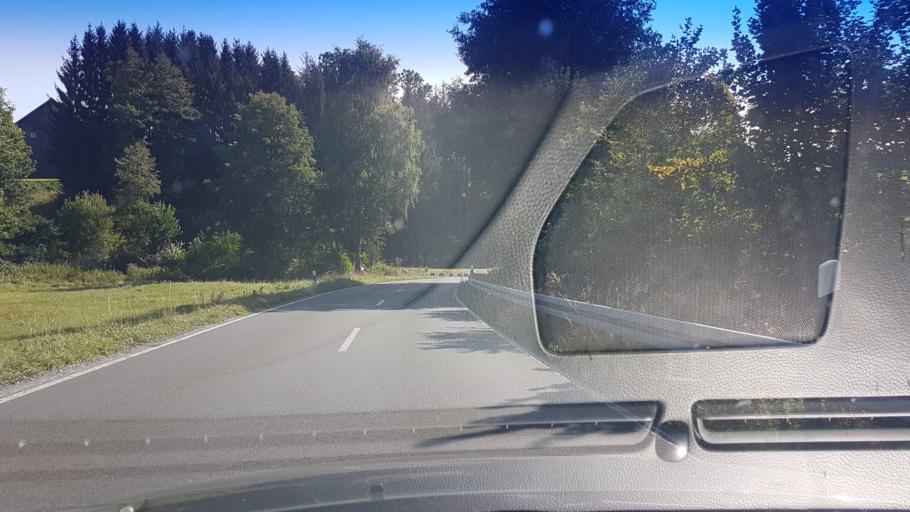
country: DE
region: Bavaria
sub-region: Upper Franconia
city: Bad Berneck im Fichtelgebirge
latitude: 50.0639
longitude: 11.6749
